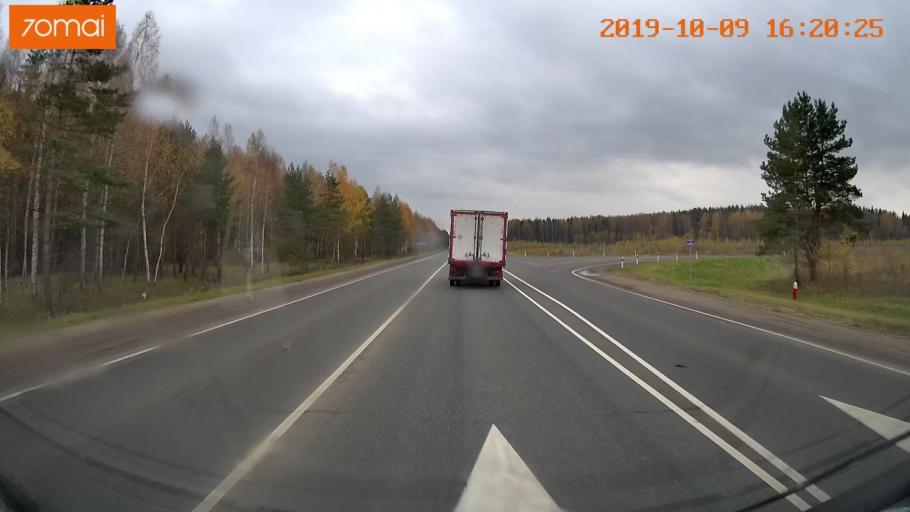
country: RU
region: Kostroma
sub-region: Kostromskoy Rayon
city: Kostroma
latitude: 57.7066
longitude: 40.8922
